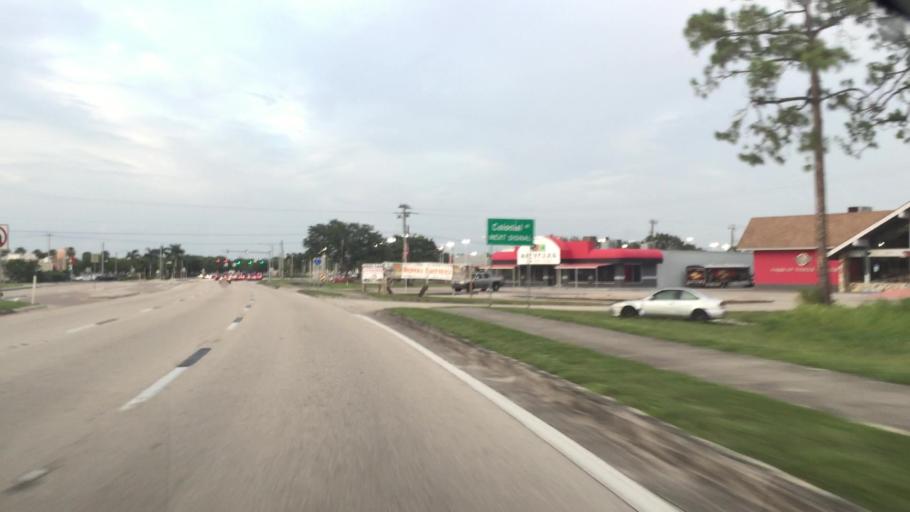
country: US
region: Florida
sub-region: Lee County
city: Pine Manor
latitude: 26.5945
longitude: -81.8642
